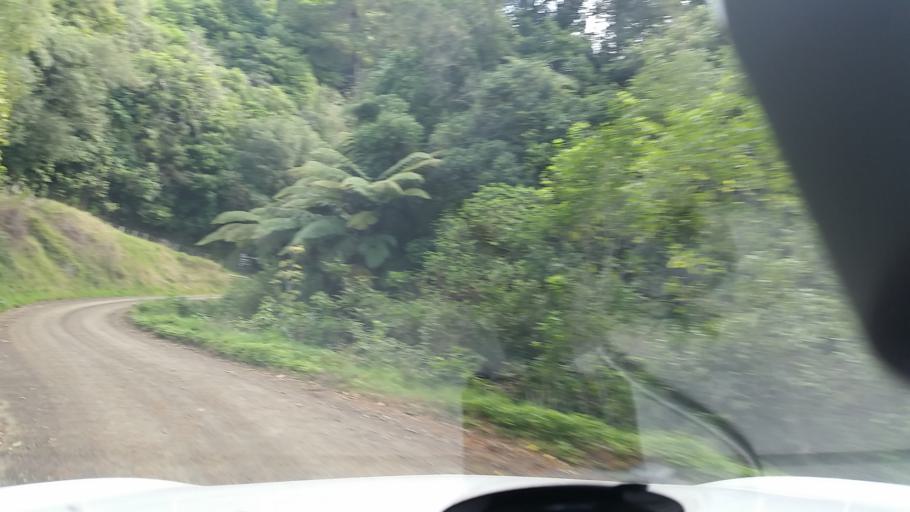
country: NZ
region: Hawke's Bay
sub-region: Napier City
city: Napier
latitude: -39.0915
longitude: 176.8708
